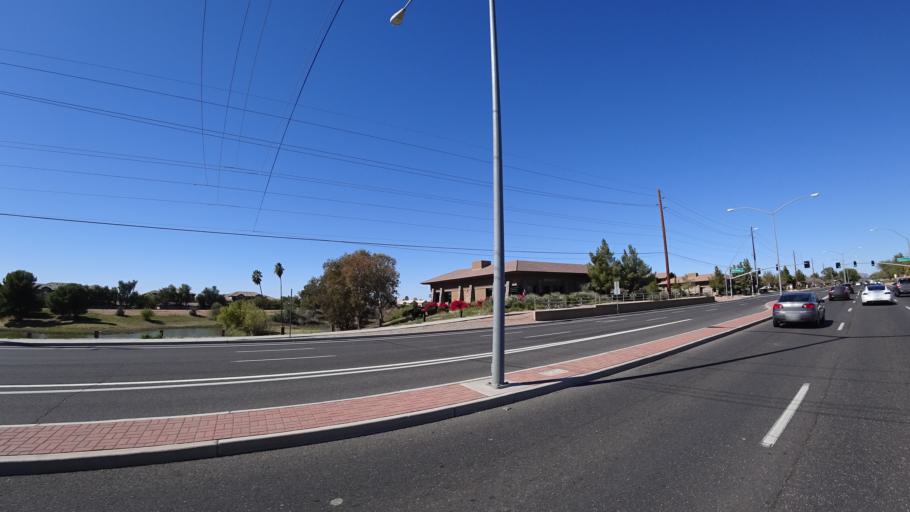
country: US
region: Arizona
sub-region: Maricopa County
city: Gilbert
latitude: 33.3674
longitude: -111.6876
